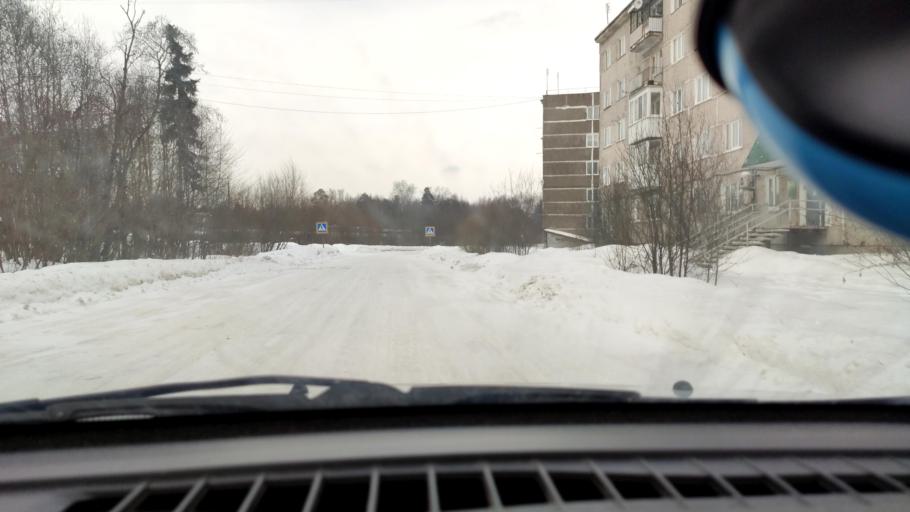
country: RU
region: Perm
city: Overyata
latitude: 58.0759
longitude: 55.8709
